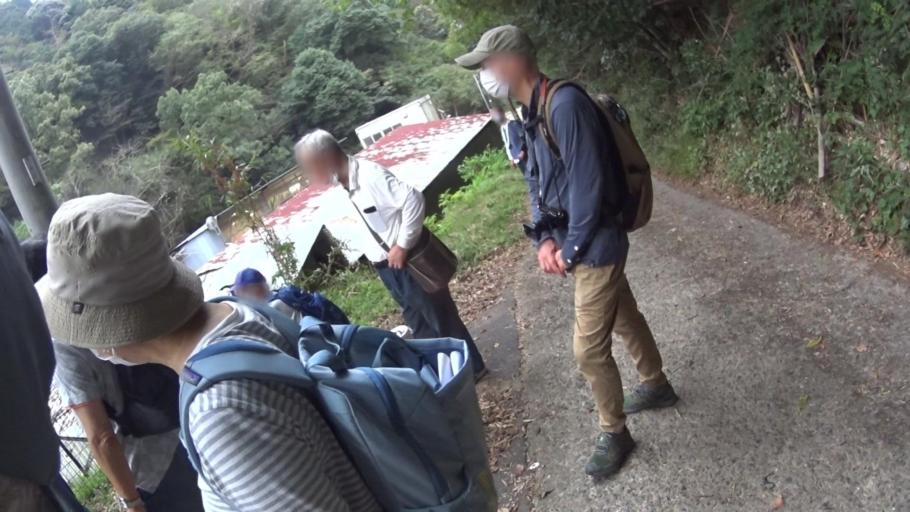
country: JP
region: Osaka
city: Kaizuka
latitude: 34.4638
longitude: 135.2965
